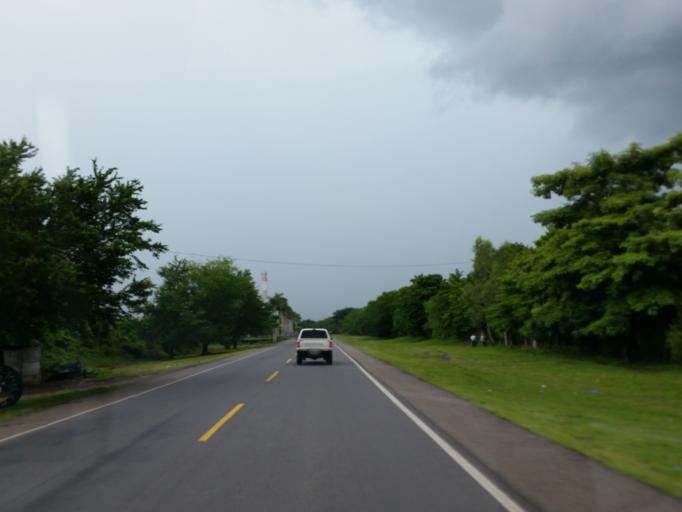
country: NI
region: Chinandega
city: Chinandega
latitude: 12.6706
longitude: -87.1137
